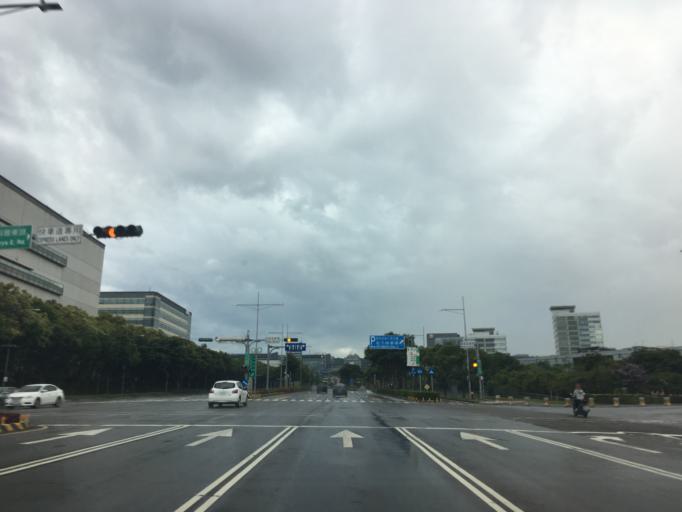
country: TW
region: Taiwan
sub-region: Taichung City
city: Taichung
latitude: 24.2073
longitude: 120.6231
